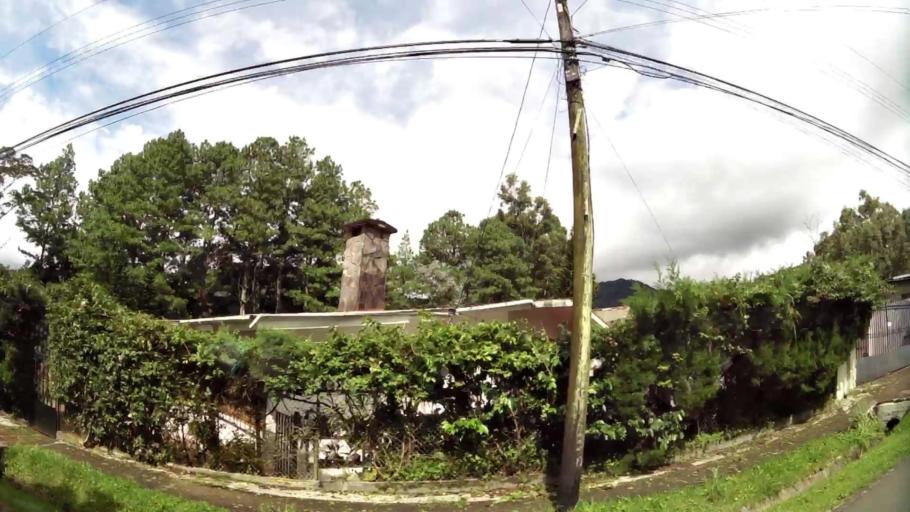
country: PA
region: Chiriqui
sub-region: Distrito Boquete
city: Boquete
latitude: 8.8002
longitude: -82.4263
